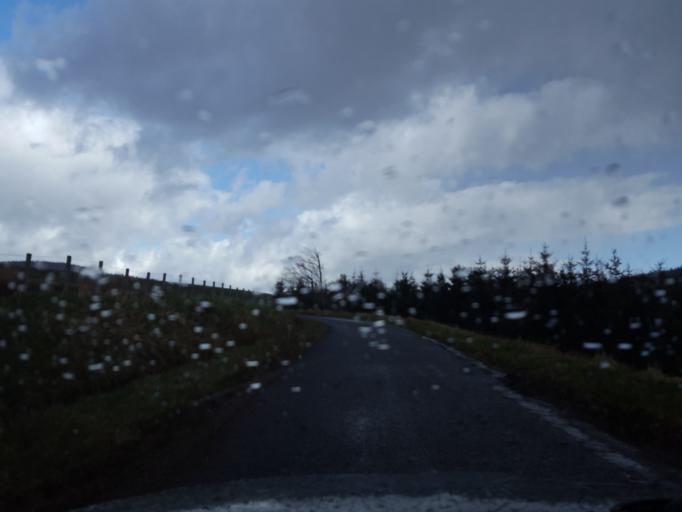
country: GB
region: Scotland
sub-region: Perth and Kinross
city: Auchterarder
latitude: 56.2587
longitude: -3.5868
